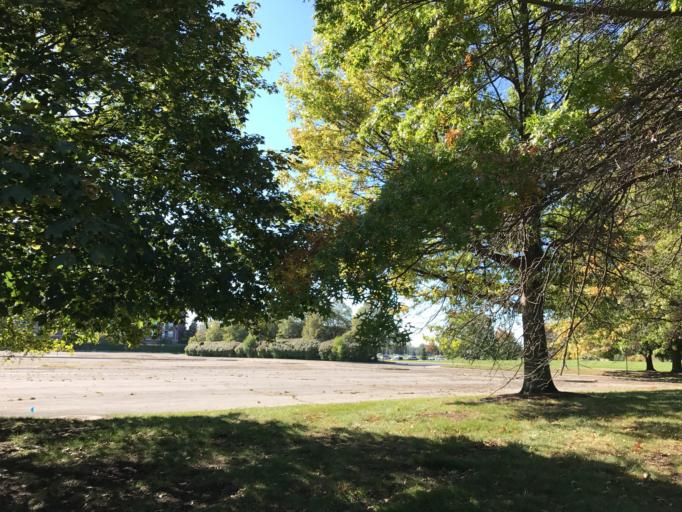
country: US
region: Michigan
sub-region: Oakland County
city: Franklin
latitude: 42.4888
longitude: -83.2967
